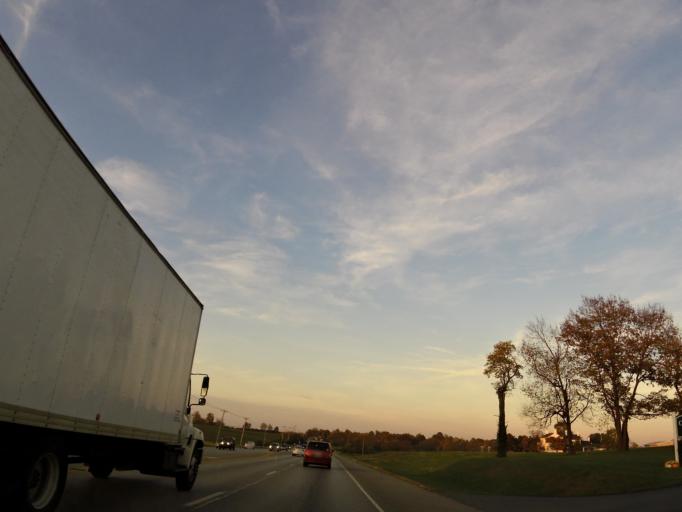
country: US
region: Kentucky
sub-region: Fayette County
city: Monticello
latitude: 37.9575
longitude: -84.5383
